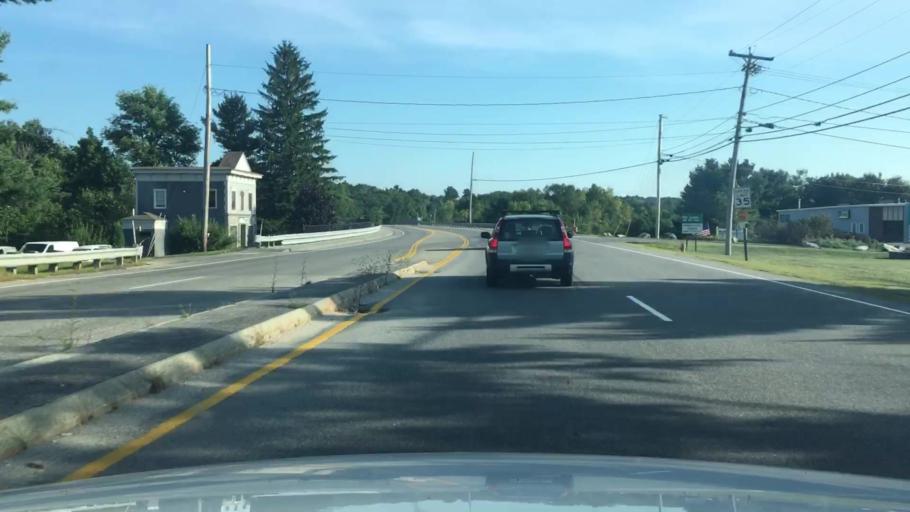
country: US
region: Maine
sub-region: Cumberland County
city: Falmouth
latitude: 43.7318
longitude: -70.2963
